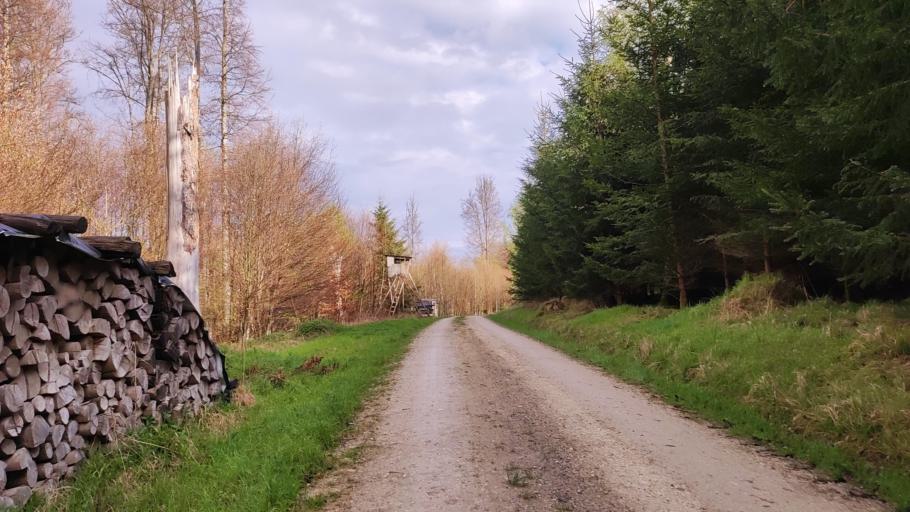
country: DE
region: Bavaria
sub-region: Swabia
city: Zusmarshausen
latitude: 48.4190
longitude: 10.6197
